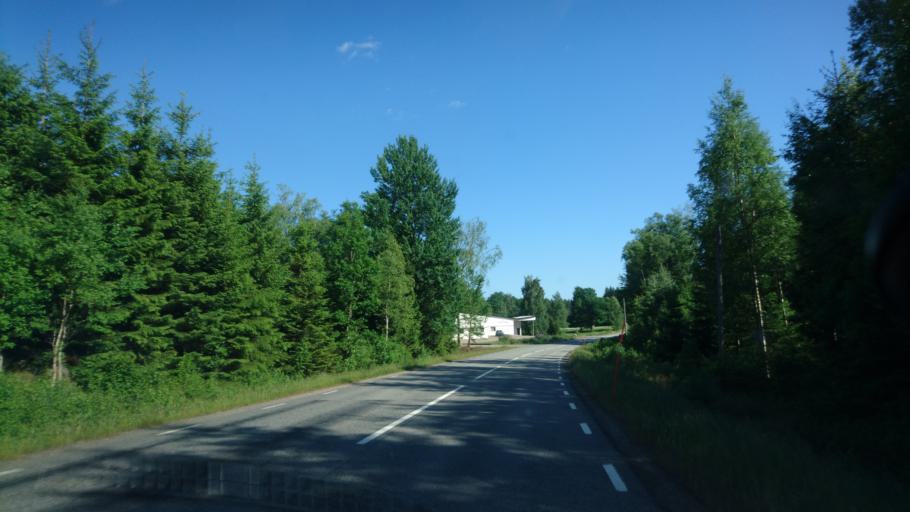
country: SE
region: Skane
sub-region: Osby Kommun
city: Lonsboda
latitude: 56.4234
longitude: 14.2822
